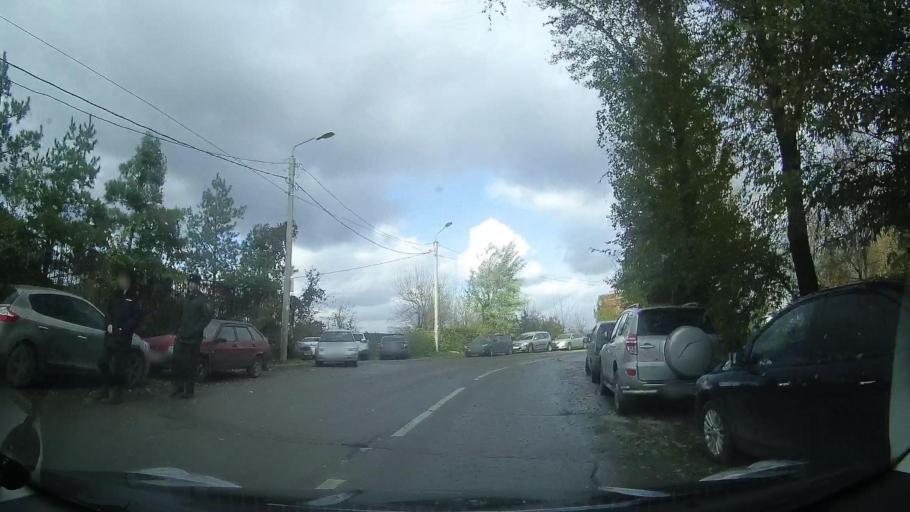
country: RU
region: Rostov
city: Severnyy
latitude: 47.2917
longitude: 39.6873
